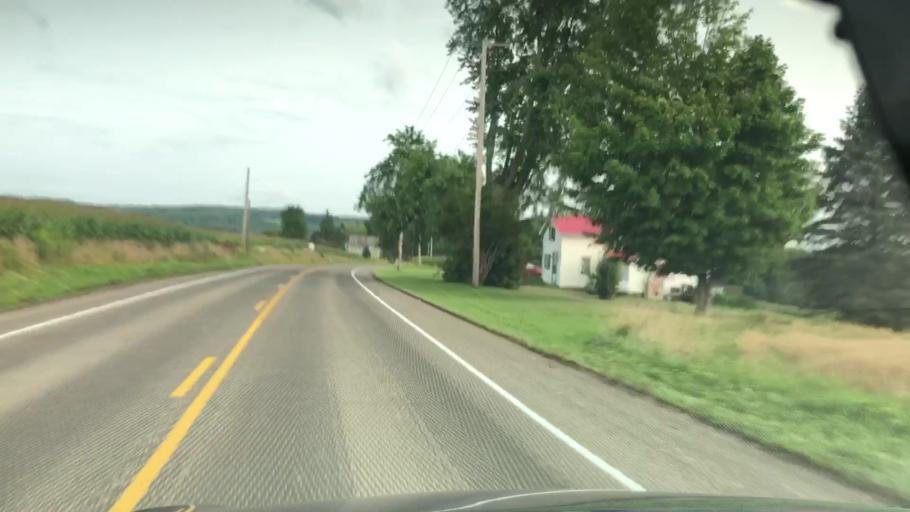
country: US
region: Pennsylvania
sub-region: Crawford County
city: Titusville
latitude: 41.7459
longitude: -79.7673
